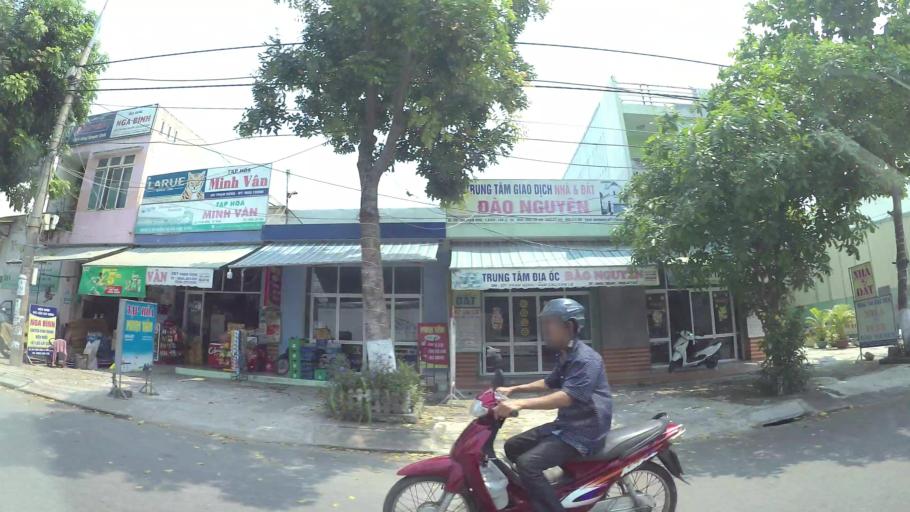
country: VN
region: Da Nang
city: Cam Le
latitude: 15.9887
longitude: 108.2078
